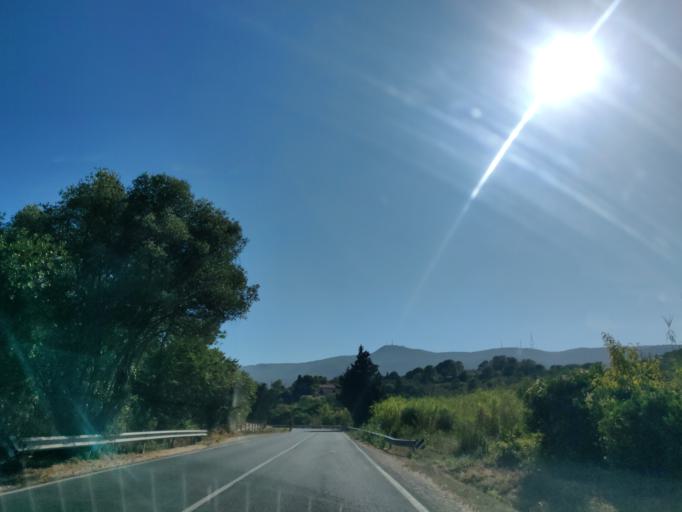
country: IT
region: Tuscany
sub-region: Provincia di Grosseto
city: Porto Ercole
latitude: 42.4097
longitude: 11.2015
